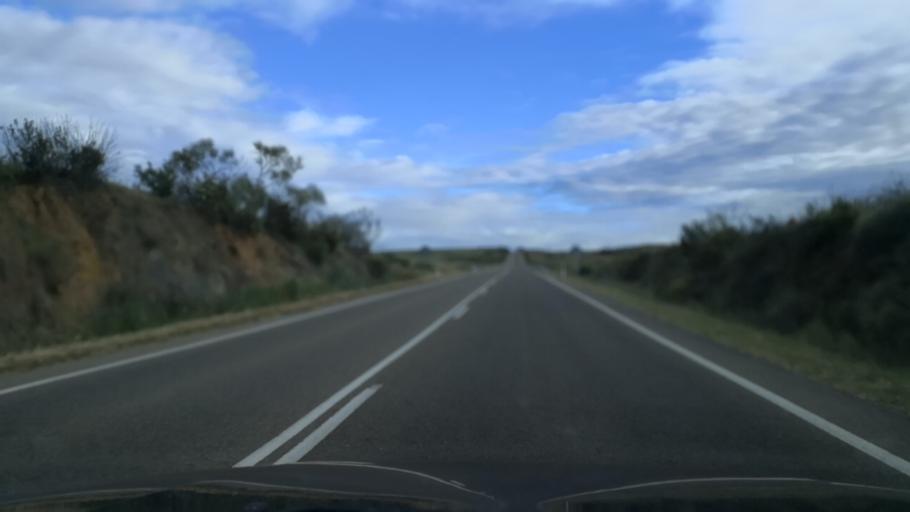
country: ES
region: Extremadura
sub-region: Provincia de Caceres
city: Coria
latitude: 39.9414
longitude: -6.5071
